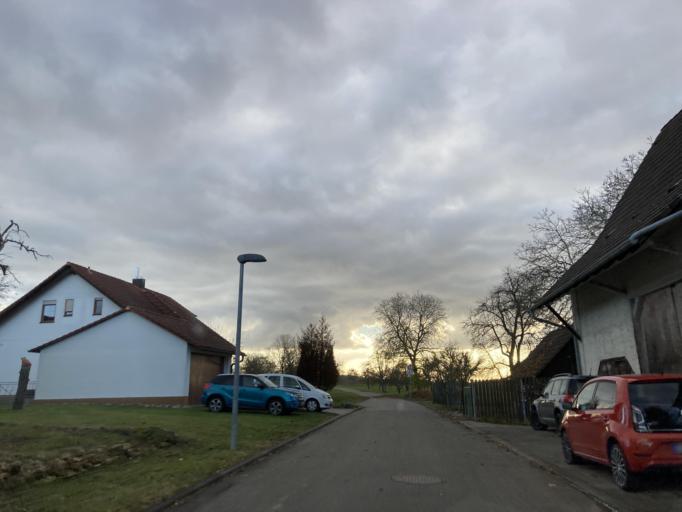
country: DE
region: Baden-Wuerttemberg
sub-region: Tuebingen Region
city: Haigerloch
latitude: 48.4285
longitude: 8.7860
